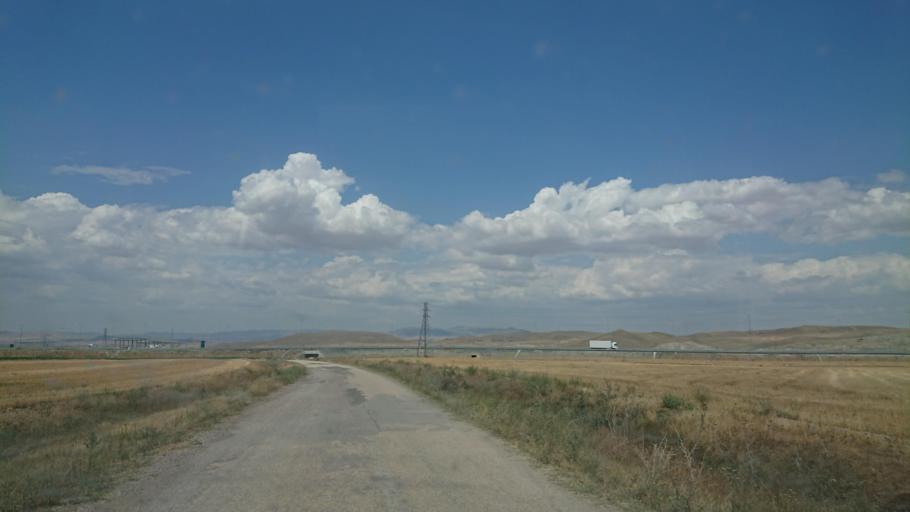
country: TR
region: Aksaray
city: Sariyahsi
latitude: 38.9714
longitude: 33.8987
